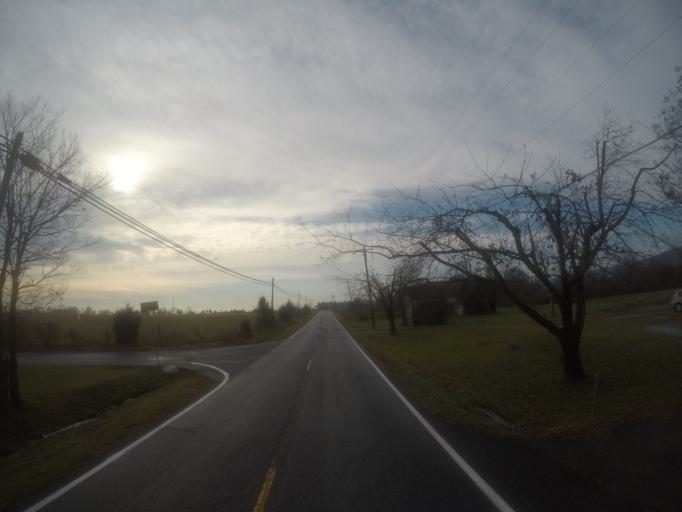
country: US
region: Maryland
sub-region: Frederick County
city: Clover Hill
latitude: 39.5201
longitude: -77.4124
